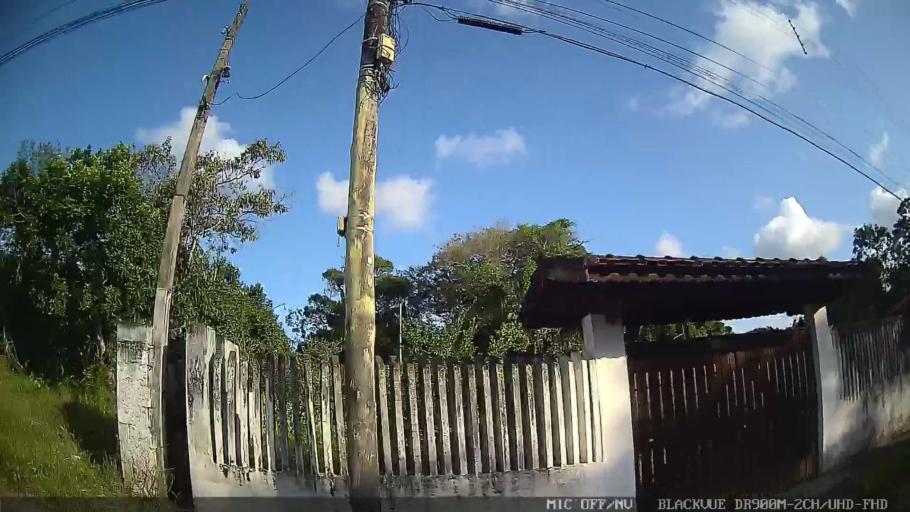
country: BR
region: Sao Paulo
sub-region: Itanhaem
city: Itanhaem
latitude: -24.1498
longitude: -46.8154
